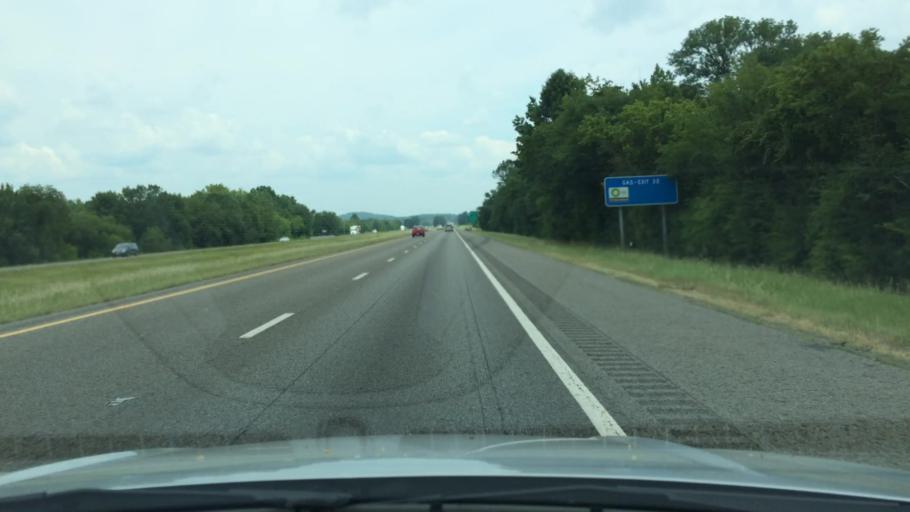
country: US
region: Tennessee
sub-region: Marshall County
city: Cornersville
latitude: 35.4305
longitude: -86.8796
